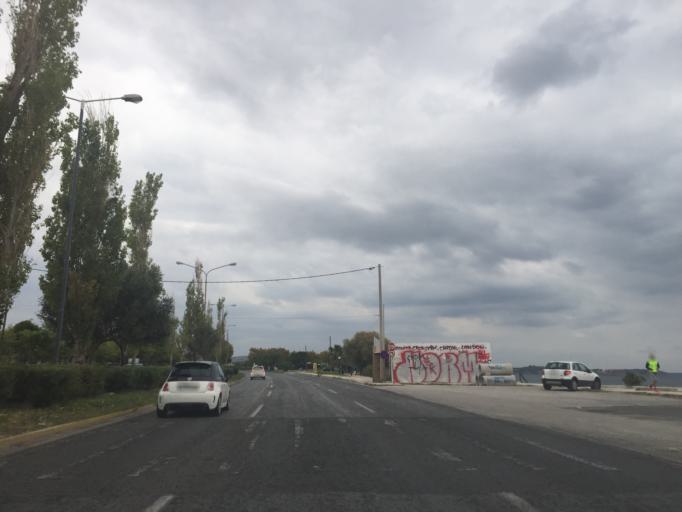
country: GR
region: Attica
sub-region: Nomarchia Athinas
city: Glyfada
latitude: 37.8459
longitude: 23.7544
